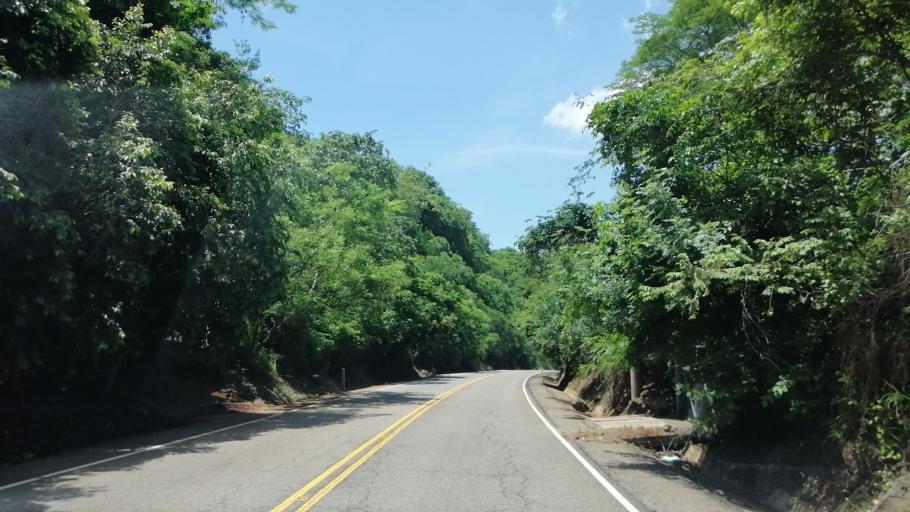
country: SV
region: Chalatenango
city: Nueva Concepcion
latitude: 14.1766
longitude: -89.3167
